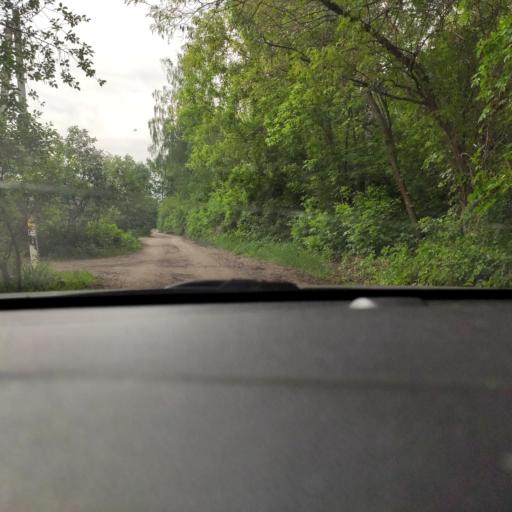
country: RU
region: Voronezj
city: Maslovka
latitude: 51.5932
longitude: 39.1671
